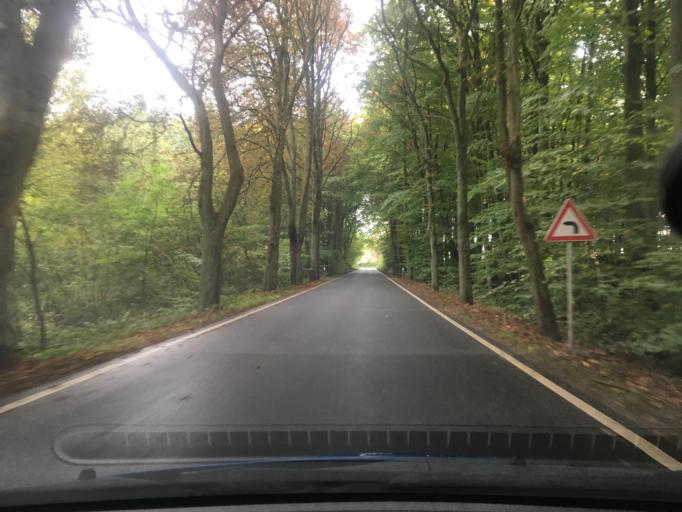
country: DE
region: Lower Saxony
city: Eyendorf
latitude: 53.1825
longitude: 10.1540
